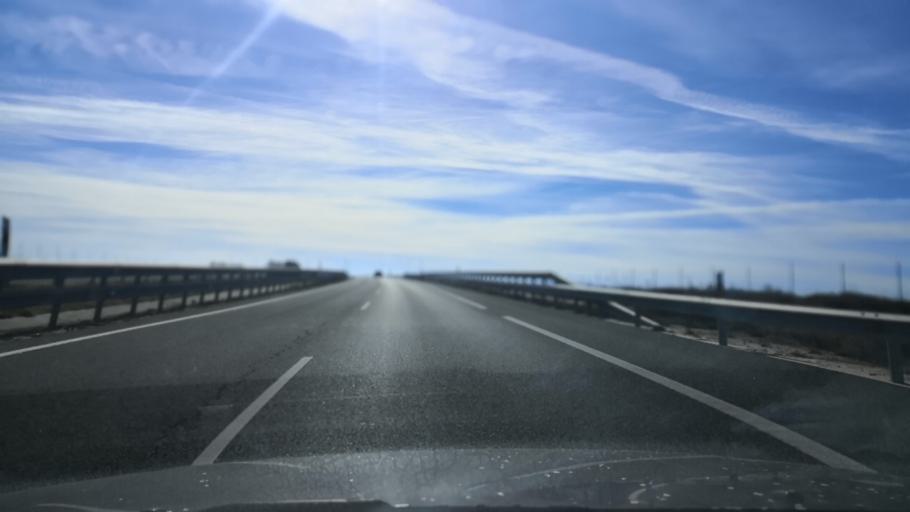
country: ES
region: Castille and Leon
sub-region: Provincia de Avila
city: Crespos
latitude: 40.8610
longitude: -4.9854
